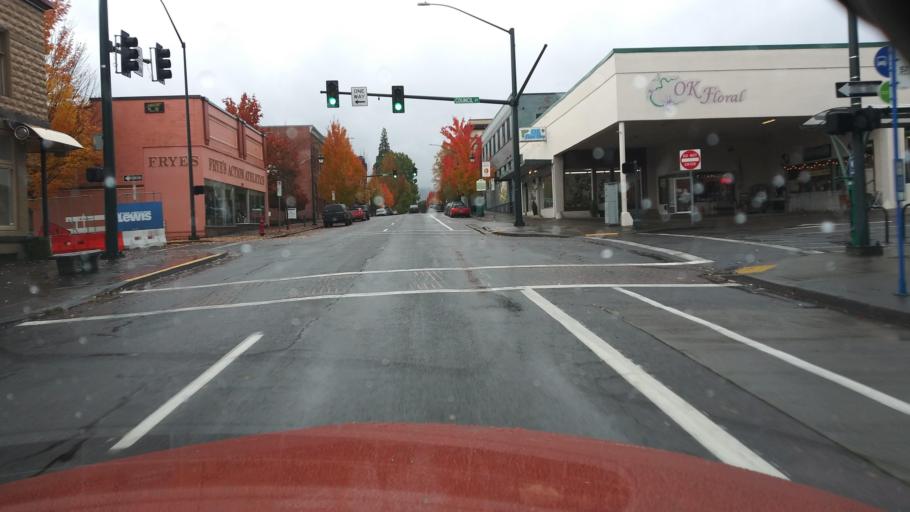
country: US
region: Oregon
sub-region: Washington County
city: Forest Grove
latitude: 45.5198
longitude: -123.1107
